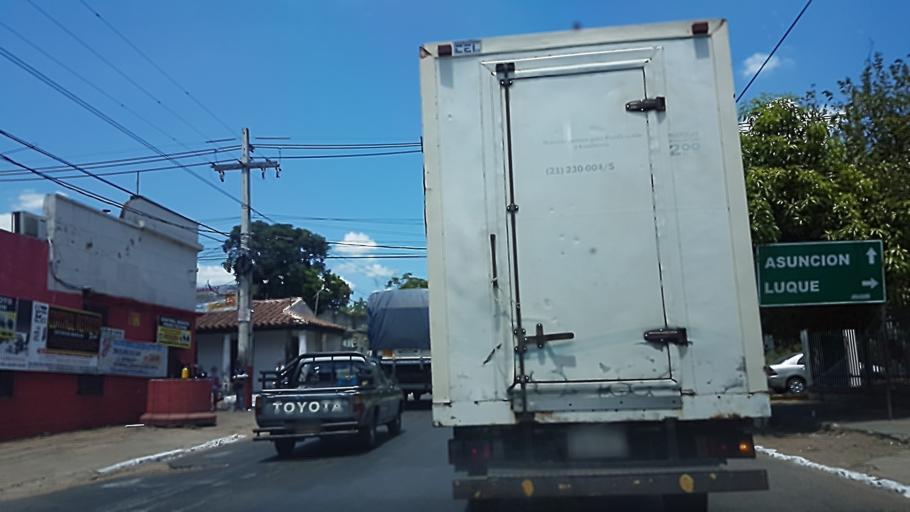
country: PY
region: Central
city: San Lorenzo
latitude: -25.3382
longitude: -57.5086
